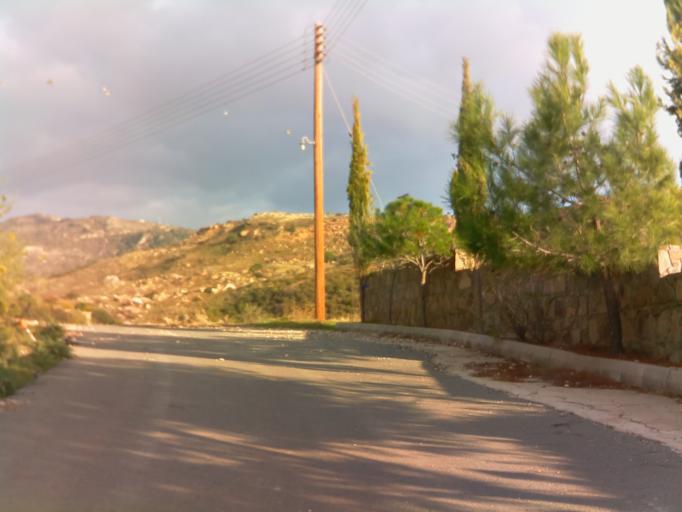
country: CY
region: Pafos
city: Kissonerga
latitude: 34.8541
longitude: 32.3987
